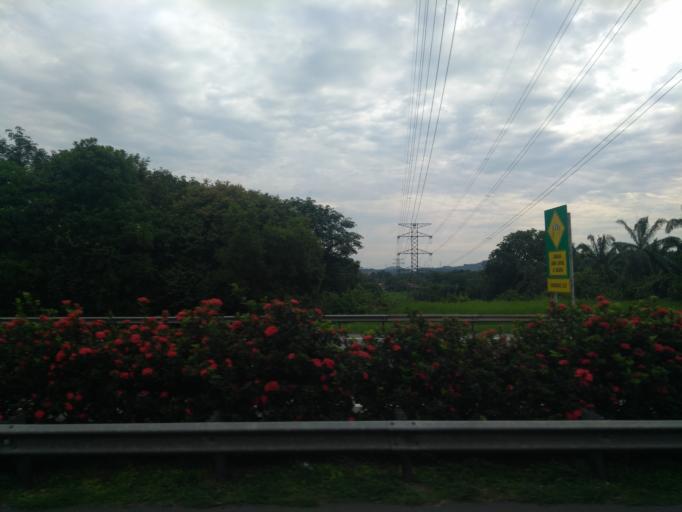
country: MY
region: Melaka
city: Alor Gajah
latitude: 2.3920
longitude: 102.2246
